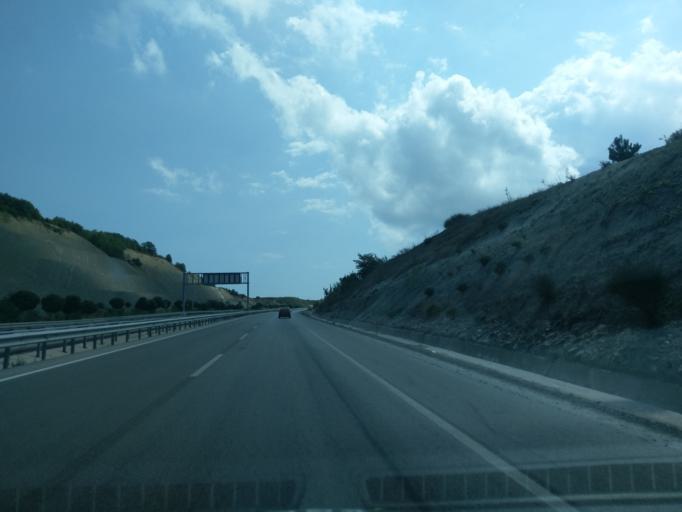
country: TR
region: Sinop
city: Kabali
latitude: 41.8562
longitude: 35.1086
